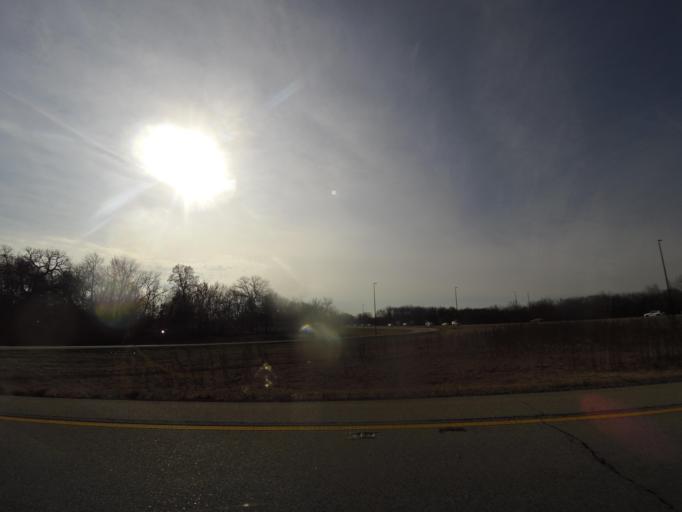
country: US
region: Illinois
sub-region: Macon County
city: Forsyth
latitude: 39.9068
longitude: -88.9542
